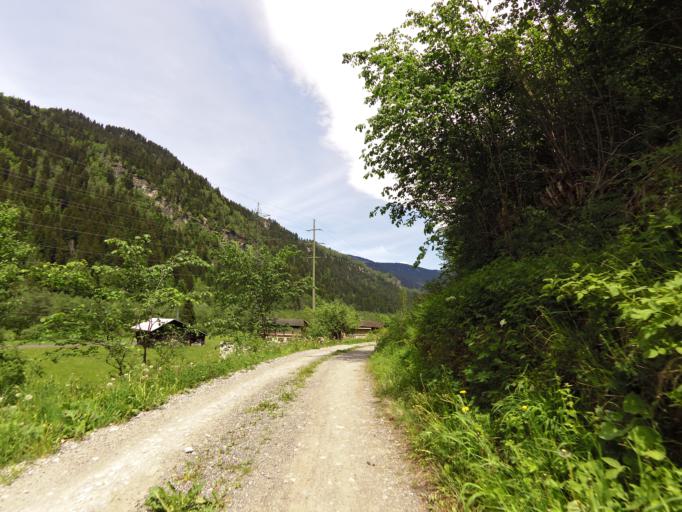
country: CH
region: Grisons
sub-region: Surselva District
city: Breil
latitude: 46.7587
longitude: 9.0949
